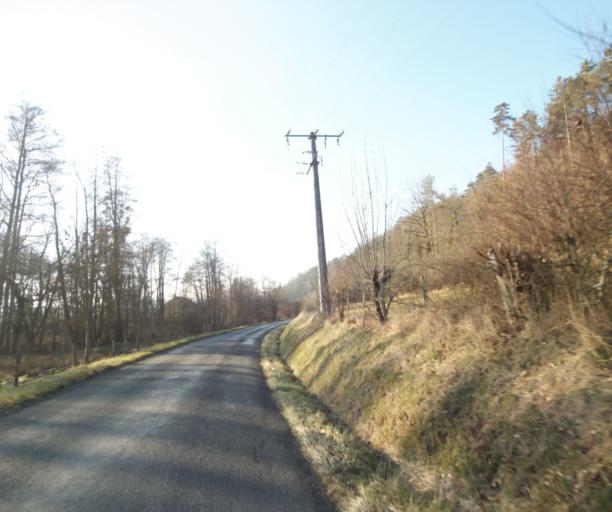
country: FR
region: Champagne-Ardenne
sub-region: Departement de la Haute-Marne
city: Chevillon
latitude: 48.4942
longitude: 5.1461
